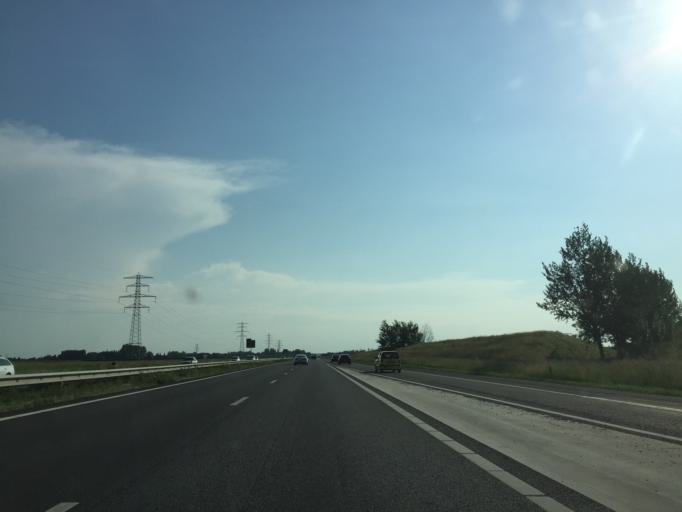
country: NL
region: Gelderland
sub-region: Gemeente Tiel
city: Tiel
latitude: 51.8903
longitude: 5.3797
